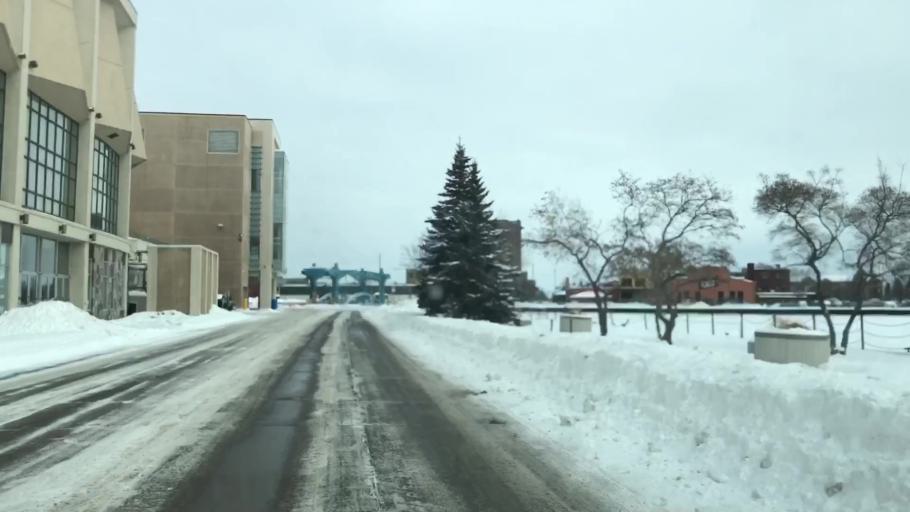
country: US
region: Minnesota
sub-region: Saint Louis County
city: Duluth
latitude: 46.7802
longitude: -92.0978
